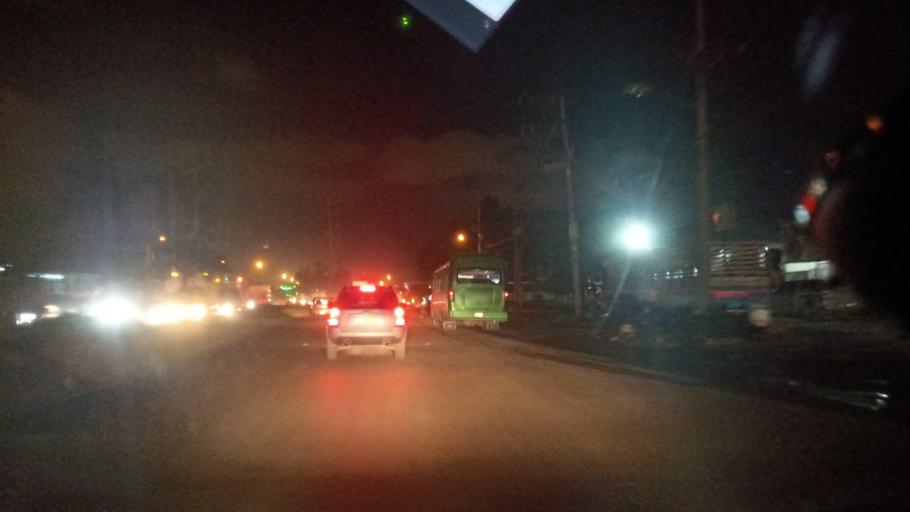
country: CO
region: Cundinamarca
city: Funza
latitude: 4.6925
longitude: -74.1671
